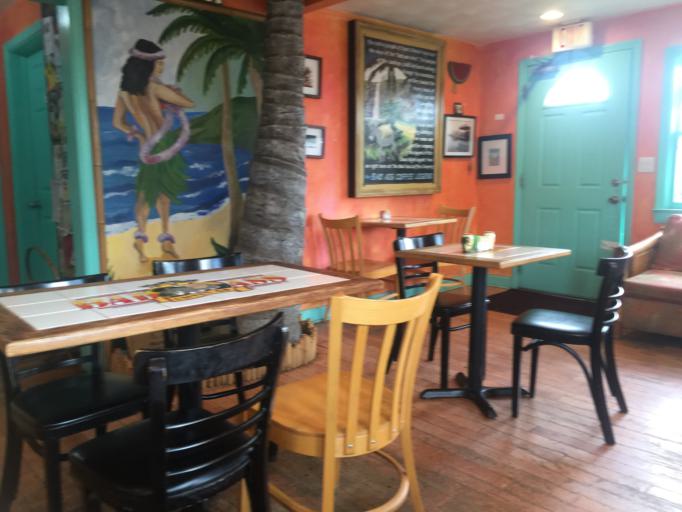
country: US
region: Virginia
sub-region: City of Virginia Beach
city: Virginia Beach
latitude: 36.8450
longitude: -75.9831
